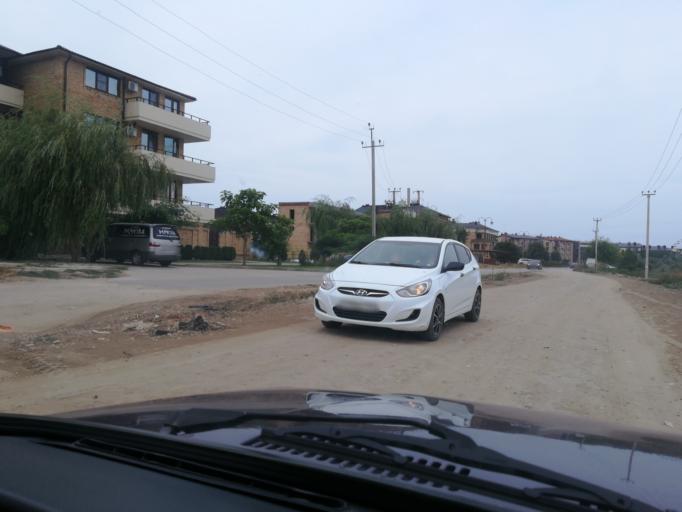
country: RU
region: Krasnodarskiy
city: Vityazevo
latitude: 44.9914
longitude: 37.2588
